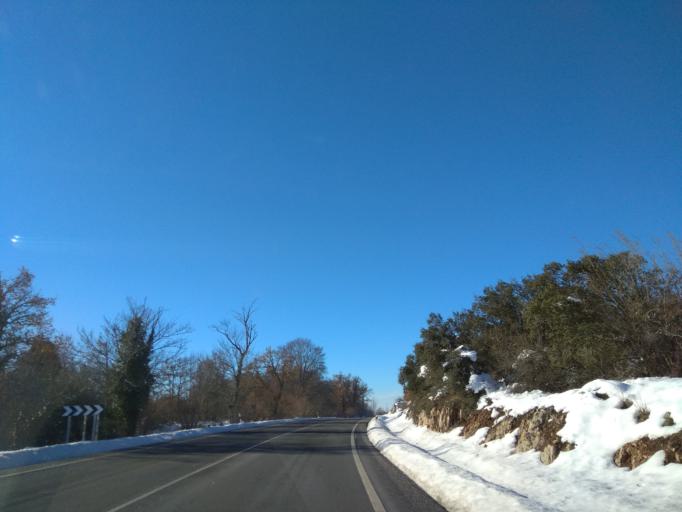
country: ES
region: Castille and Leon
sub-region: Provincia de Burgos
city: Espinosa de los Monteros
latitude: 42.9396
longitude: -3.6971
